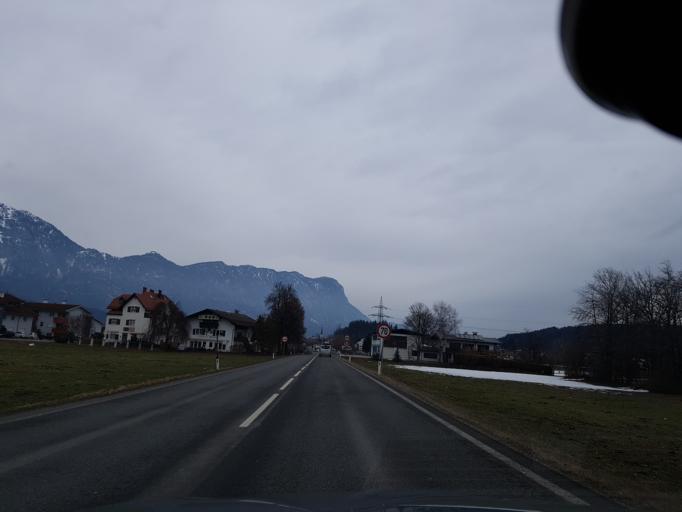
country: AT
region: Tyrol
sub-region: Politischer Bezirk Kufstein
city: Angath
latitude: 47.4997
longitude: 12.0829
